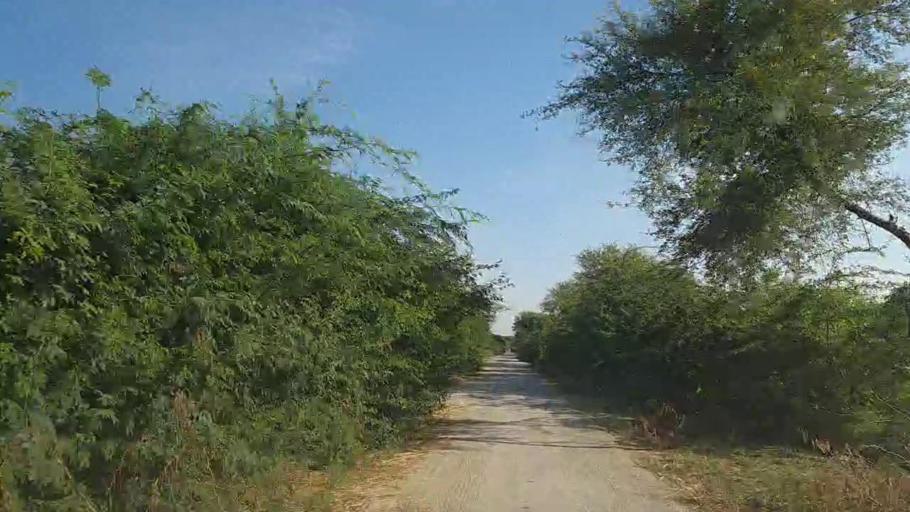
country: PK
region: Sindh
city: Bulri
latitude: 24.7915
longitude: 68.3447
